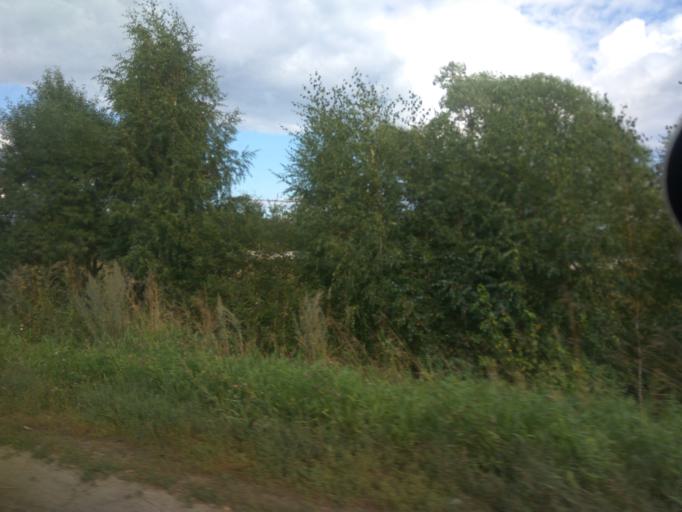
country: RU
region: Moskovskaya
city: Bronnitsy
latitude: 55.4803
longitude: 38.2338
